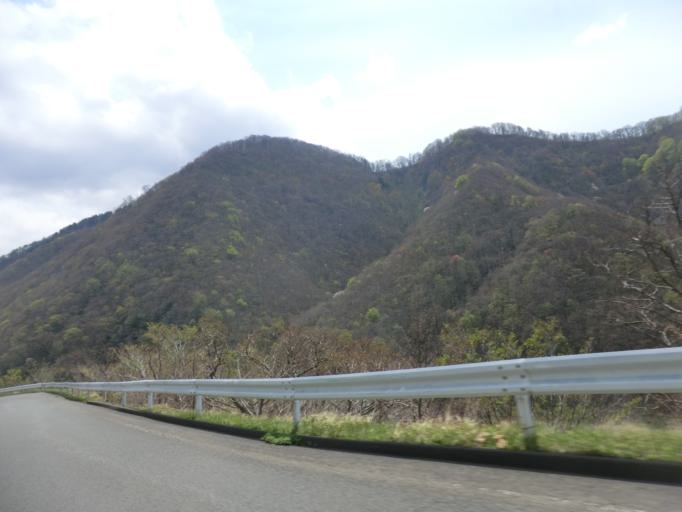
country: JP
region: Aomori
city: Mutsu
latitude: 41.2883
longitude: 140.8099
